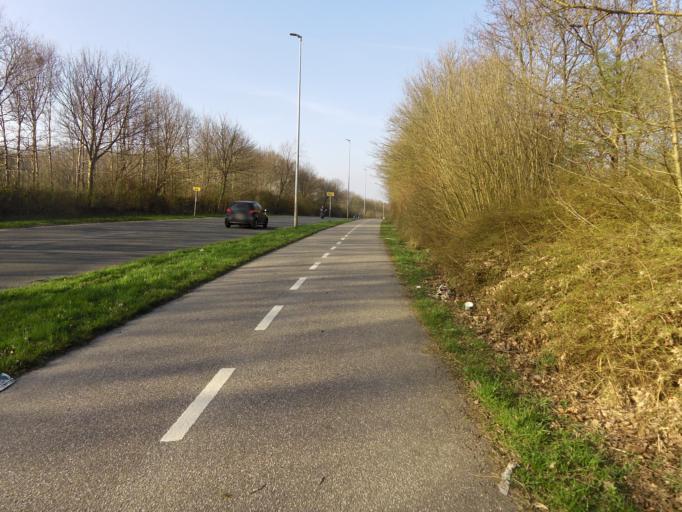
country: DK
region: South Denmark
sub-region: Vejen Kommune
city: Vejen
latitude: 55.4851
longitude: 9.1260
